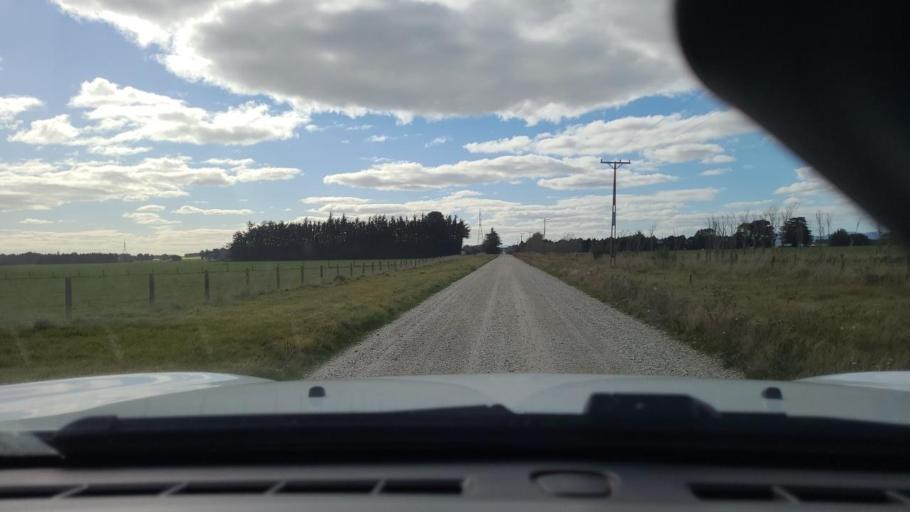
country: NZ
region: Southland
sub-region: Invercargill City
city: Invercargill
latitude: -46.3042
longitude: 168.5564
